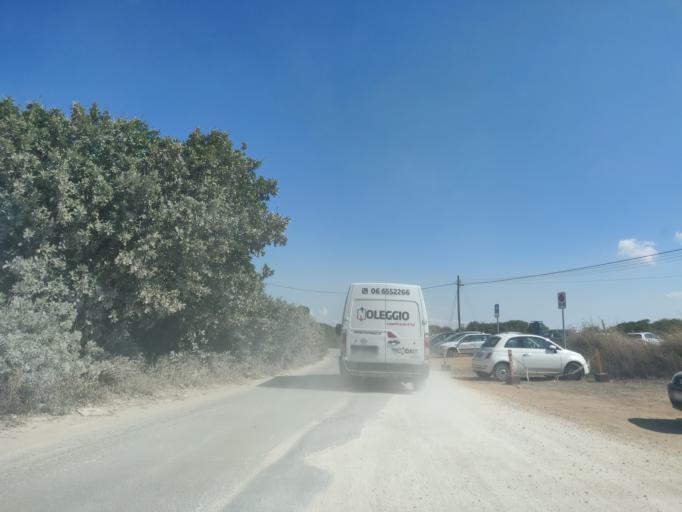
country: IT
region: Latium
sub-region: Citta metropolitana di Roma Capitale
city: Aurelia
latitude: 42.1695
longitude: 11.7411
